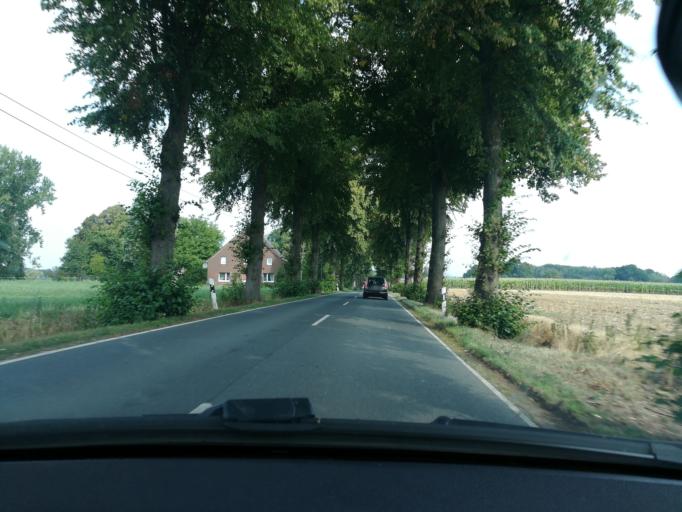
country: DE
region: Lower Saxony
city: Melle
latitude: 52.1525
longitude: 8.3329
